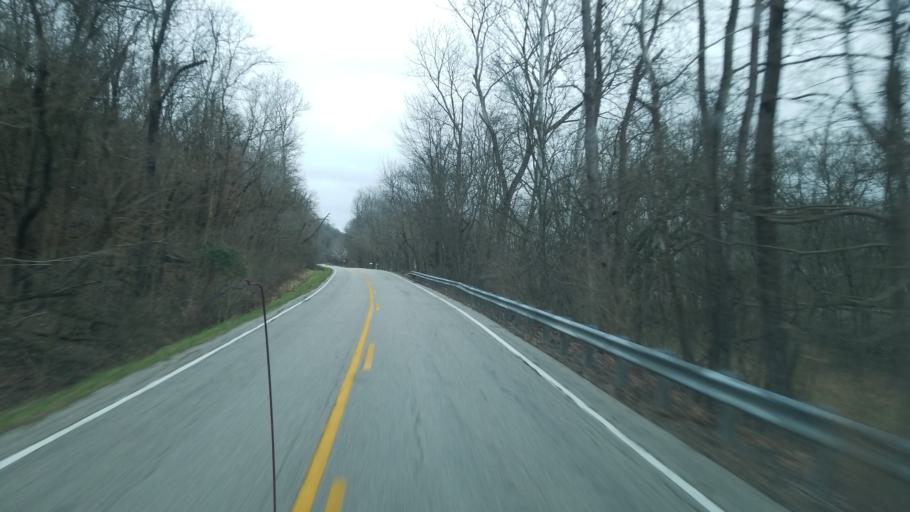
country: US
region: Kentucky
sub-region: Bracken County
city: Augusta
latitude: 38.7674
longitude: -84.0861
